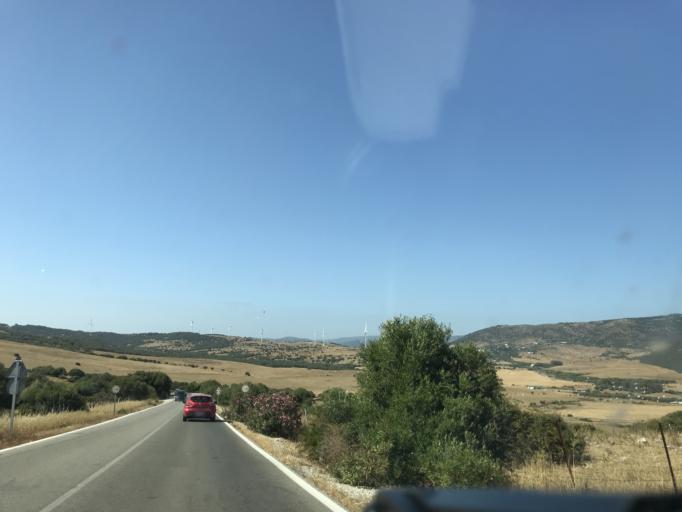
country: ES
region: Andalusia
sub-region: Provincia de Cadiz
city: Zahara de los Atunes
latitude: 36.1016
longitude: -5.7201
